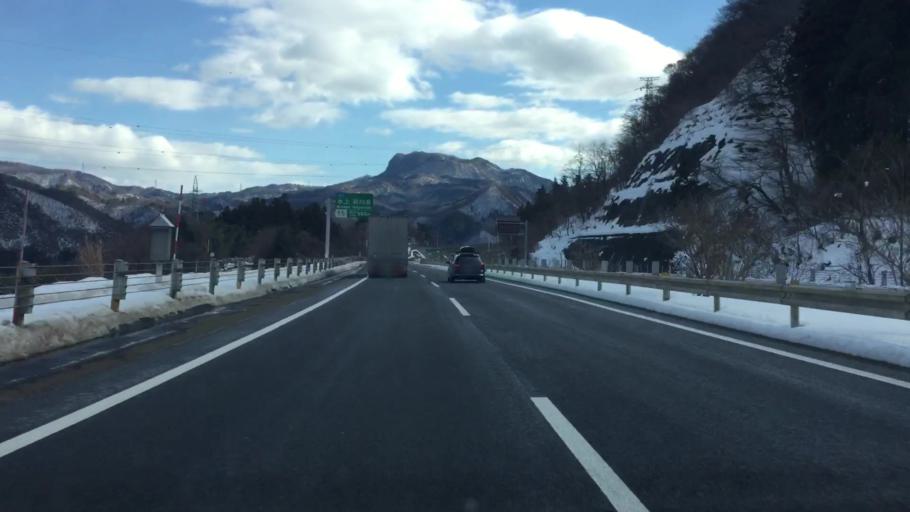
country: JP
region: Gunma
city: Numata
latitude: 36.7525
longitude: 138.9695
